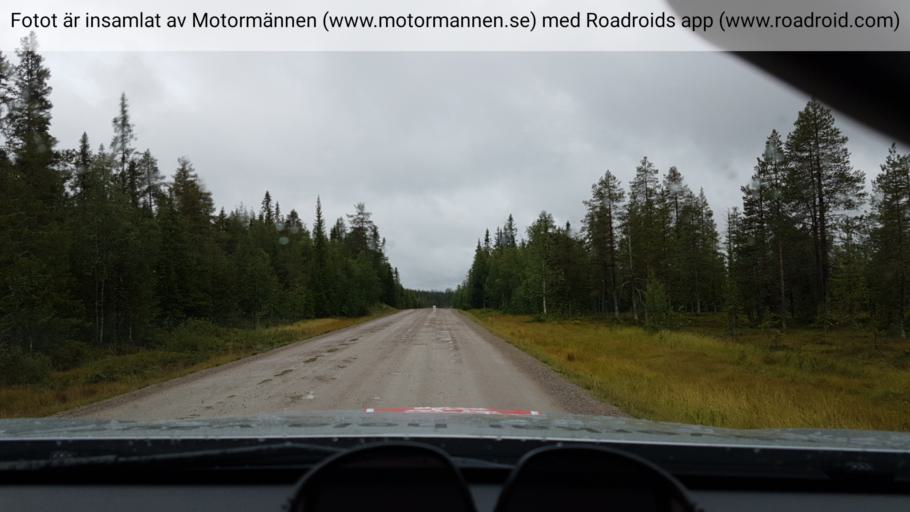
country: SE
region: Vaesterbotten
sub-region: Lycksele Kommun
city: Soderfors
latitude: 64.7629
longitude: 17.6586
